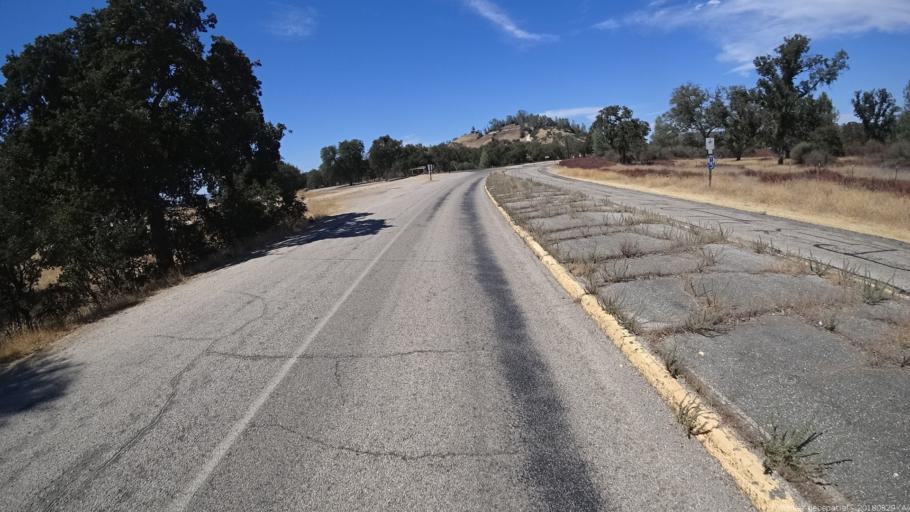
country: US
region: California
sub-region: Monterey County
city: King City
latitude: 35.9682
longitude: -121.1758
